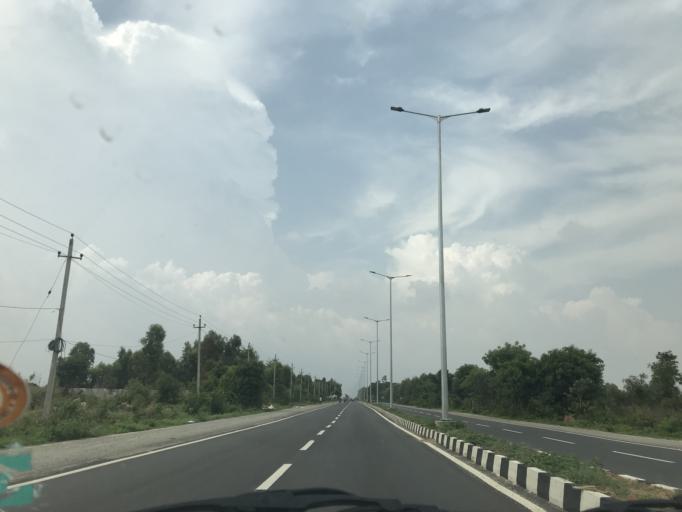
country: IN
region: Karnataka
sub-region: Bangalore Rural
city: Devanhalli
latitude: 13.1581
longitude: 77.6826
